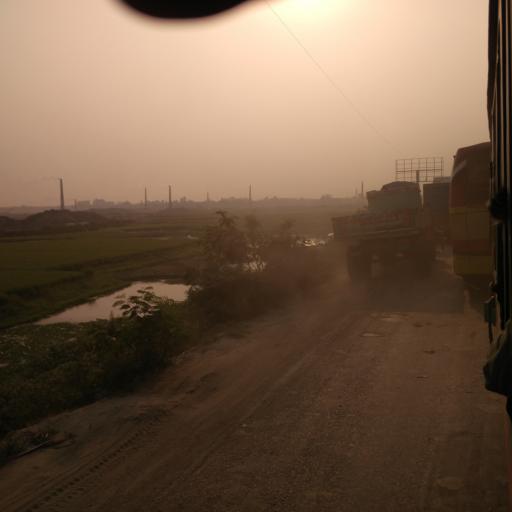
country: BD
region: Dhaka
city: Tungi
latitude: 23.8948
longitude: 90.3468
